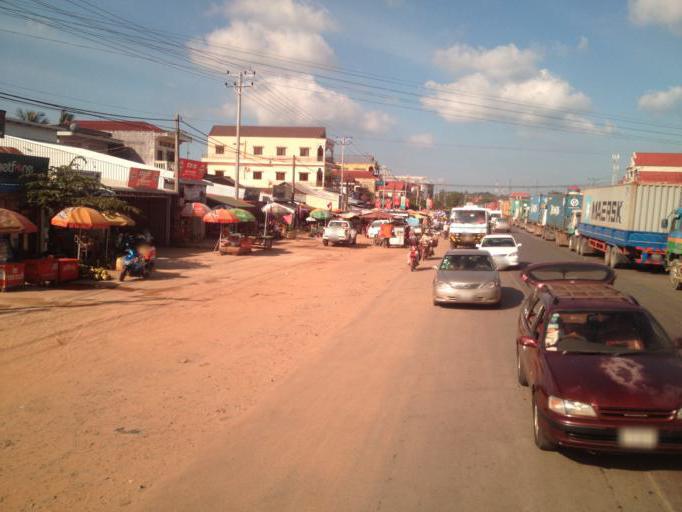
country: KH
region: Preah Sihanouk
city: Sihanoukville
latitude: 10.6348
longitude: 103.5387
